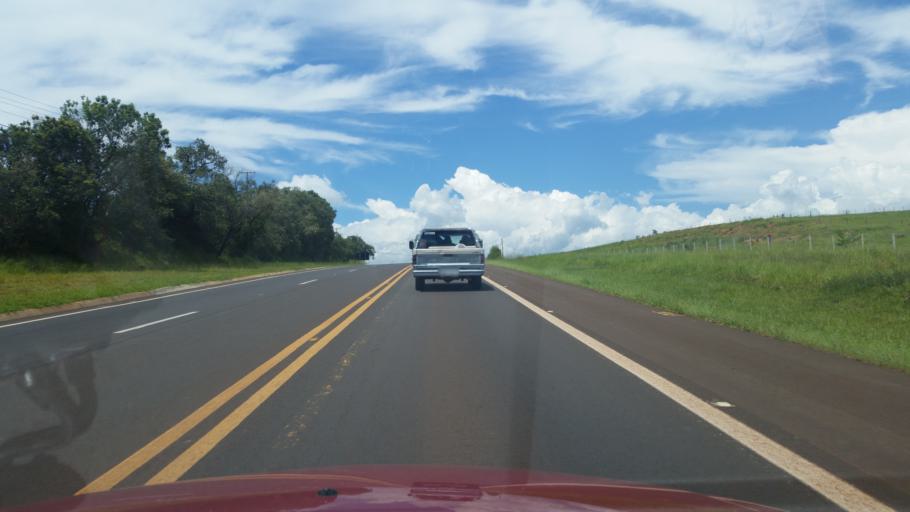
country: BR
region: Sao Paulo
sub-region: Itai
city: Itai
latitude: -23.2843
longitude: -49.0297
